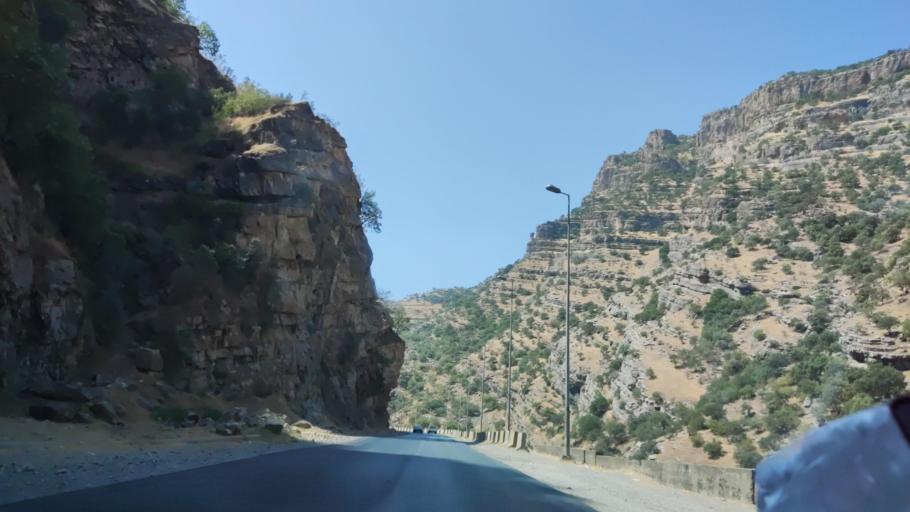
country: IQ
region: Arbil
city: Ruwandiz
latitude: 36.6437
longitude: 44.4945
